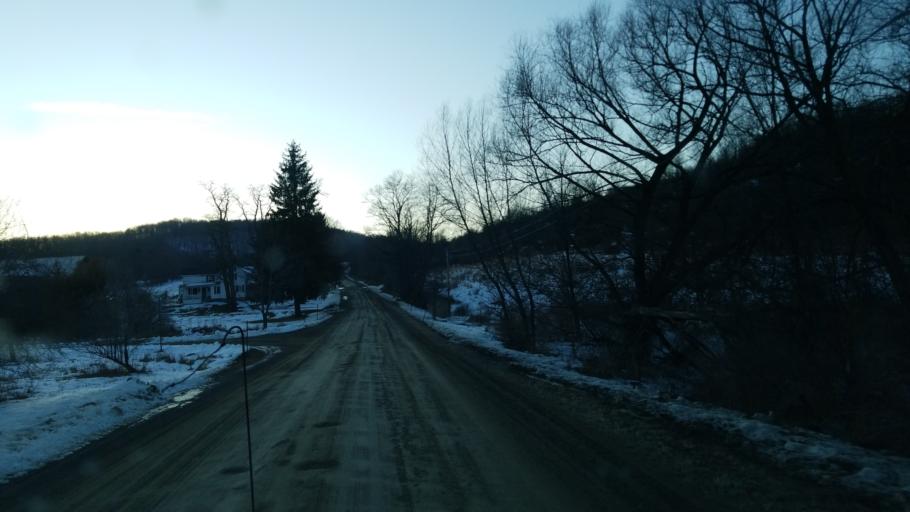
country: US
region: Pennsylvania
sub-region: Tioga County
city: Westfield
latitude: 42.0369
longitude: -77.5793
